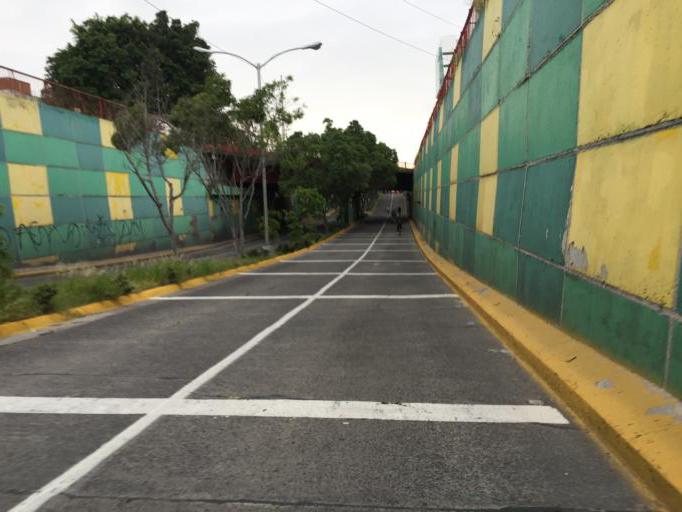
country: MX
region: Jalisco
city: Guadalajara
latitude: 20.6666
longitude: -103.3800
